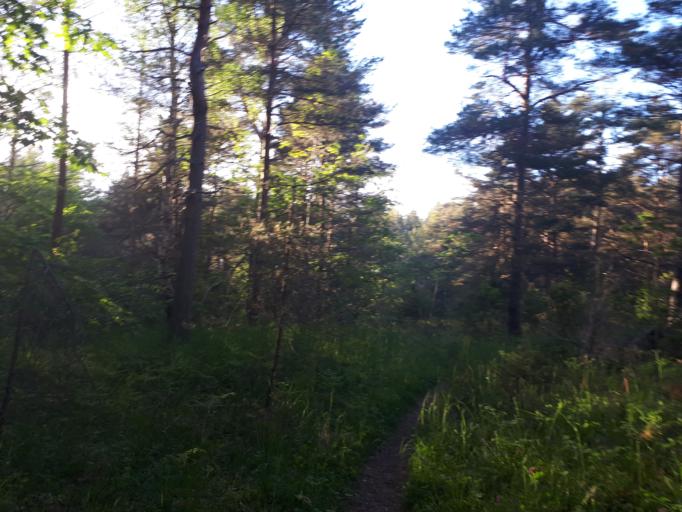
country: SE
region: Gotland
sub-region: Gotland
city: Visby
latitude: 57.6071
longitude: 18.2885
